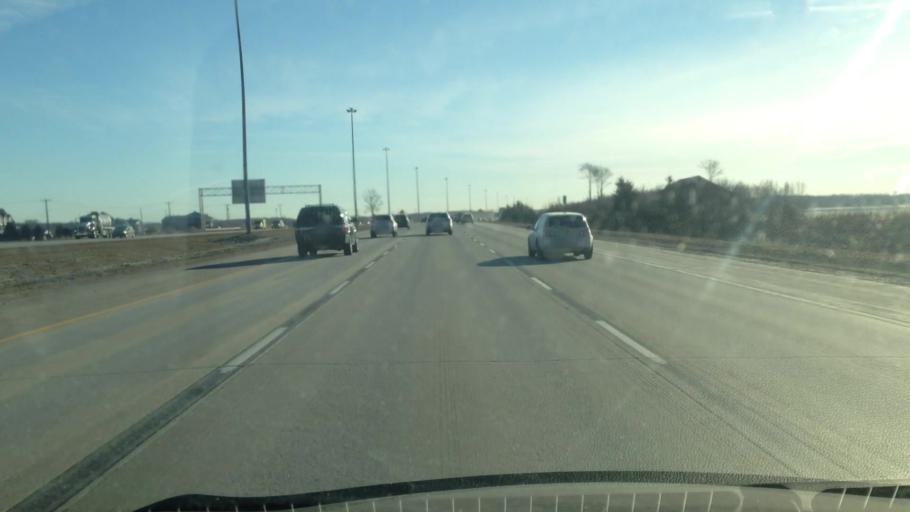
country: CA
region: Quebec
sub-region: Laurentides
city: Saint-Jerome
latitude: 45.7362
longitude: -73.9875
